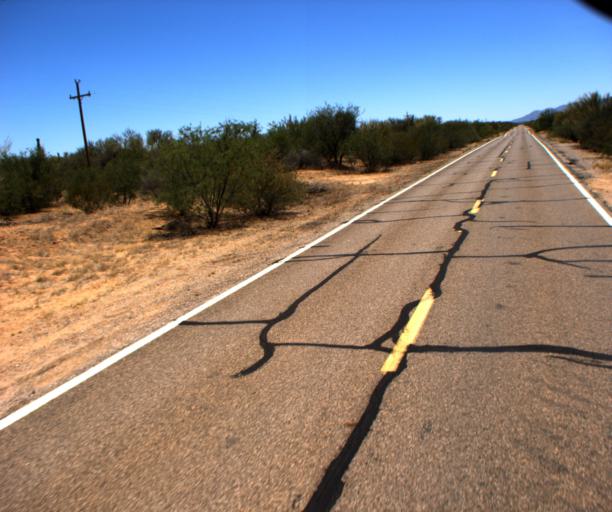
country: US
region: Arizona
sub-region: Pima County
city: Three Points
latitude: 31.9934
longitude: -111.3668
